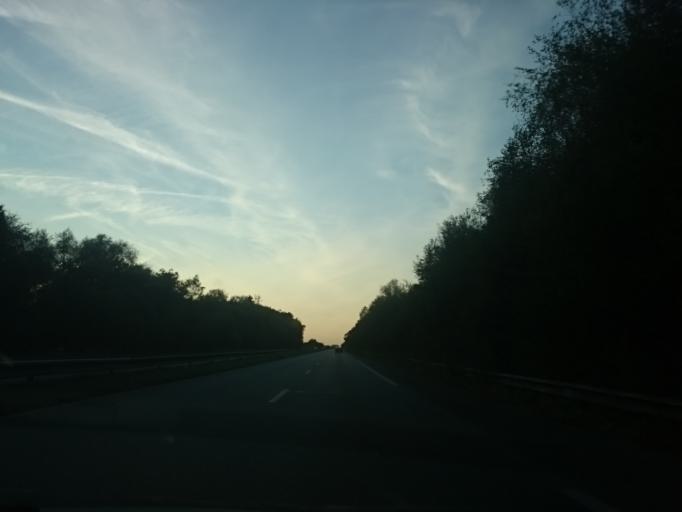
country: FR
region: Brittany
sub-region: Departement du Finistere
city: Redene
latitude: 47.8286
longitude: -3.4774
